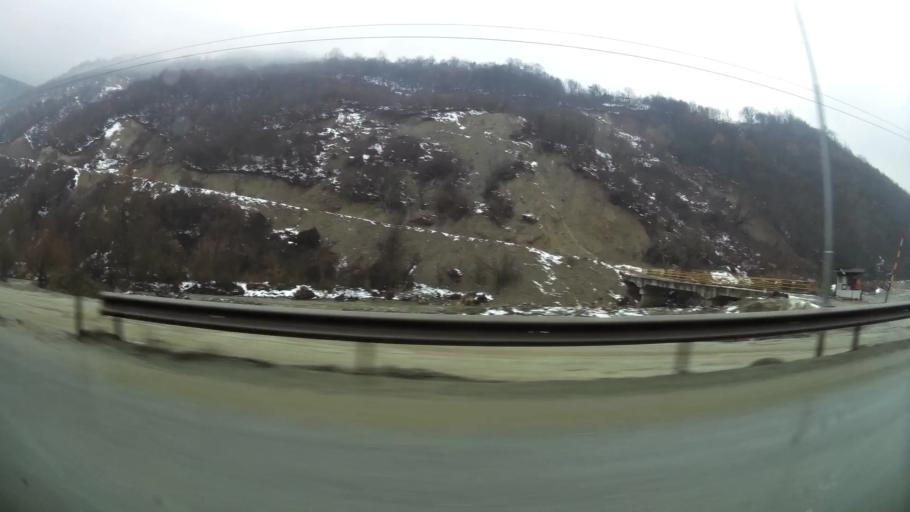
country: XK
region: Ferizaj
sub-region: Hani i Elezit
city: Hani i Elezit
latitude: 42.1658
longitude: 21.2770
